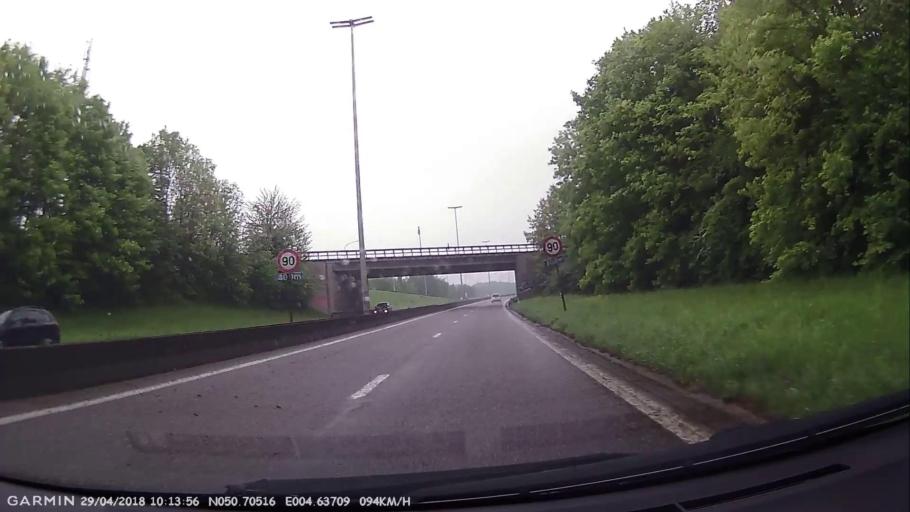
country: BE
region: Wallonia
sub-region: Province du Brabant Wallon
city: Wavre
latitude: 50.7049
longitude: 4.6369
